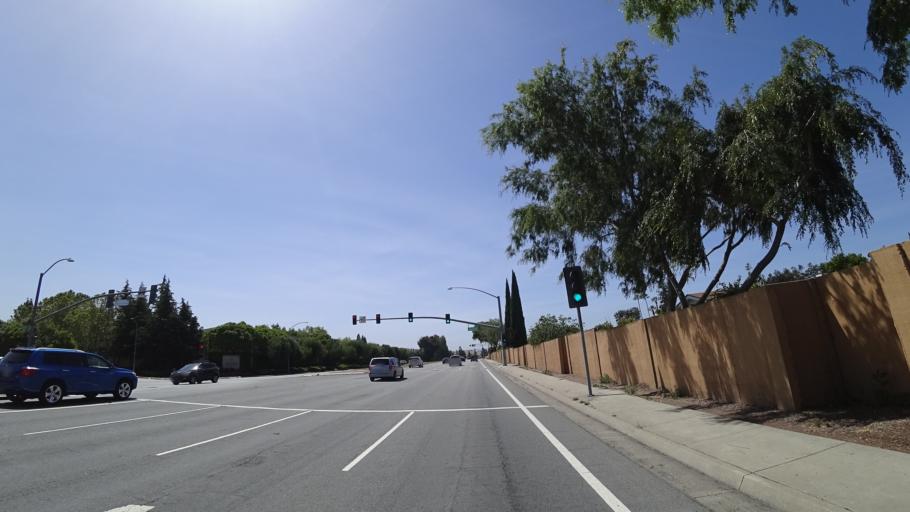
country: US
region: California
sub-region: Santa Clara County
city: Seven Trees
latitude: 37.3166
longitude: -121.8082
